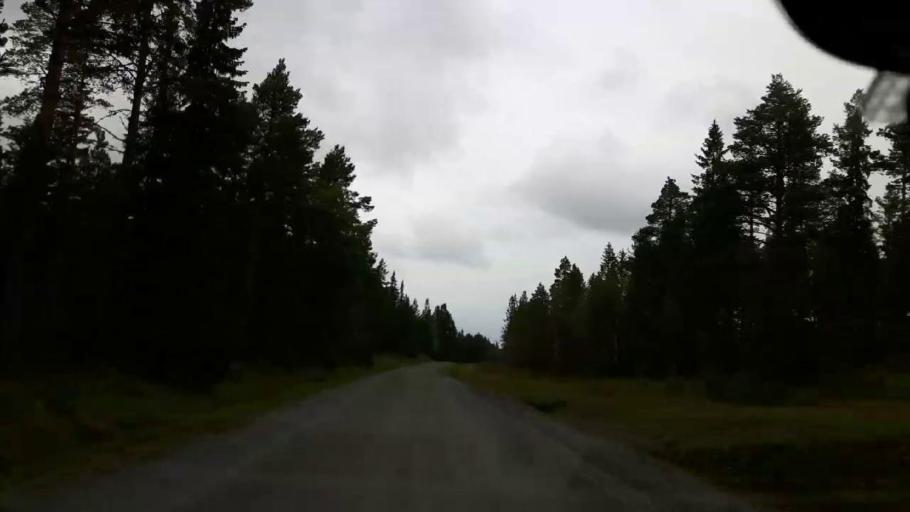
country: SE
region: Jaemtland
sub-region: OEstersunds Kommun
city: Ostersund
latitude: 63.0805
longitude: 14.5551
